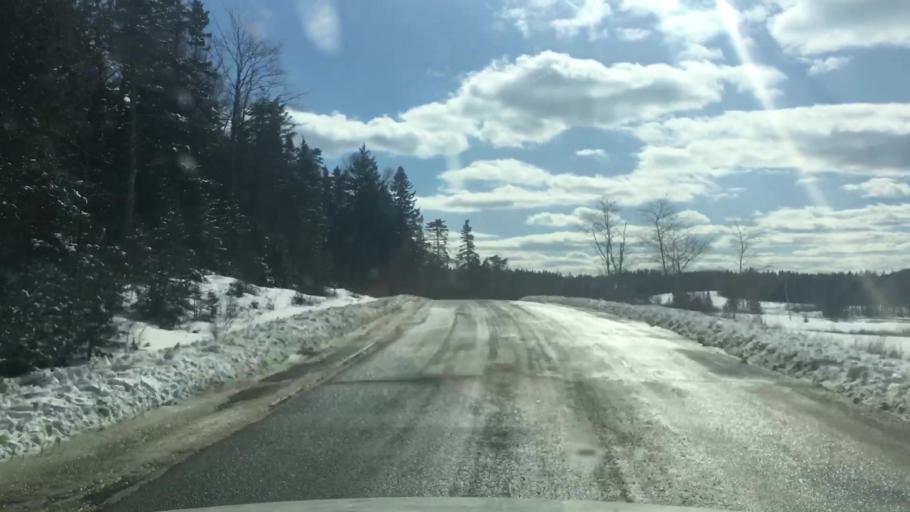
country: US
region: Maine
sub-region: Washington County
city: Machiasport
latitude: 44.6725
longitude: -67.4227
